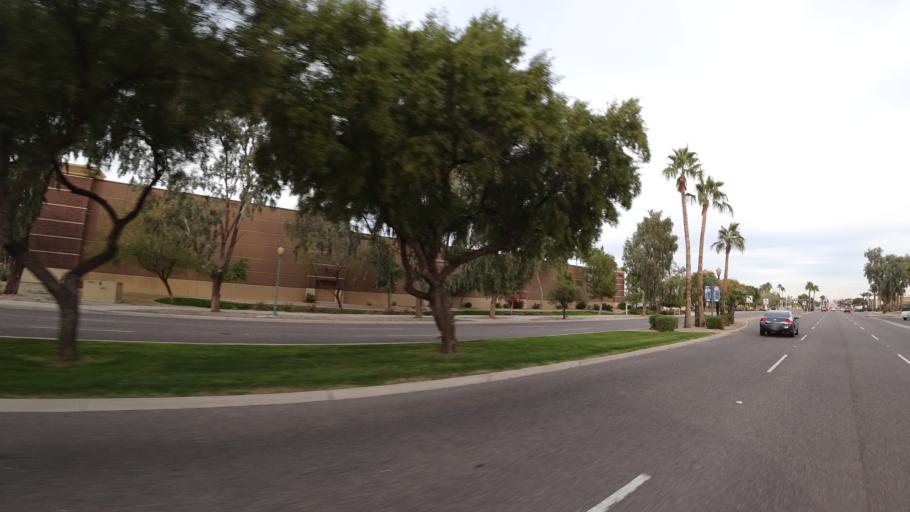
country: US
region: Arizona
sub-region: Maricopa County
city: Surprise
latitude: 33.6386
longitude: -112.3625
